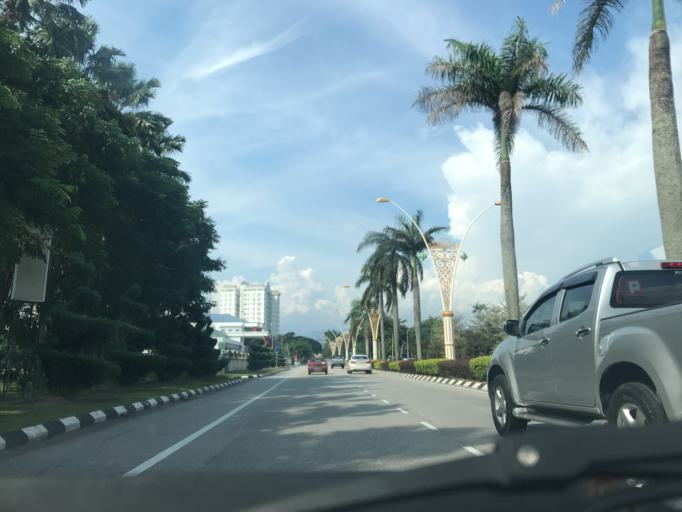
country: MY
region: Perak
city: Ipoh
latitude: 4.5937
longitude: 101.0942
